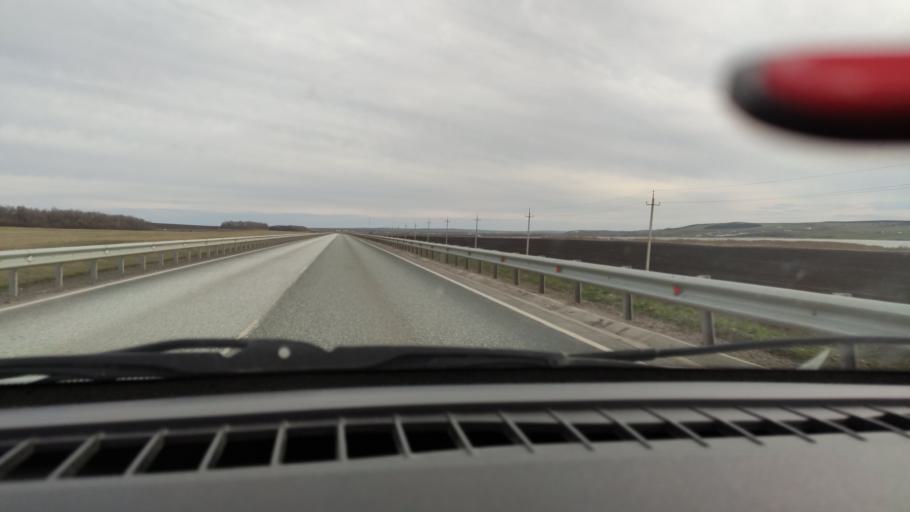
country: RU
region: Bashkortostan
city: Yermolayevo
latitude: 52.5136
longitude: 55.8308
